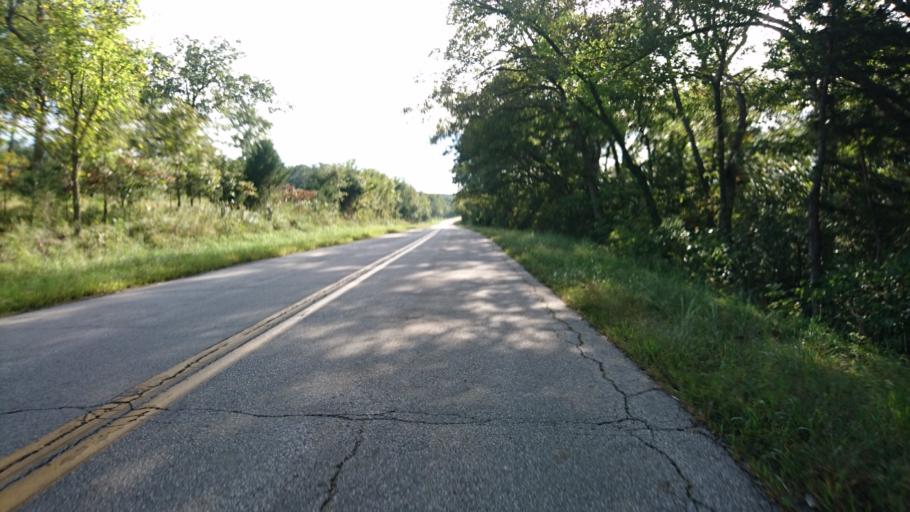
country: US
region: Missouri
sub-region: Crawford County
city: Cuba
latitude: 38.1025
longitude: -91.3484
